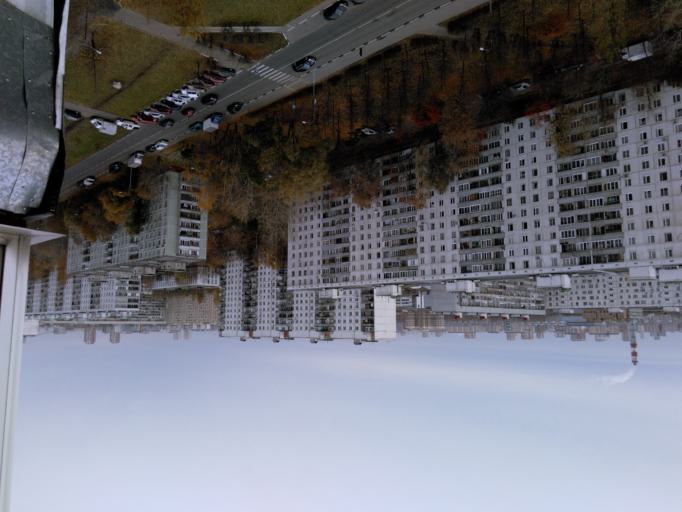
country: RU
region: Moscow
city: Slobodka
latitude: 55.8585
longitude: 37.5909
